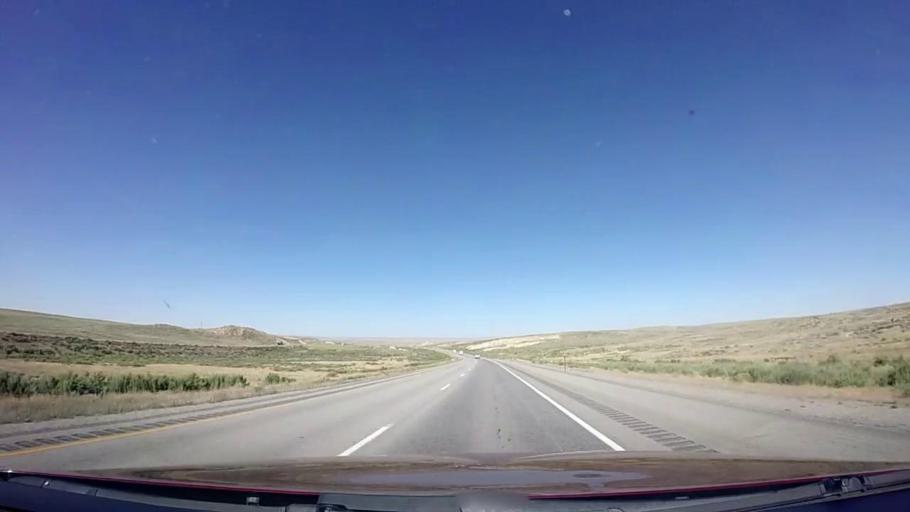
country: US
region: Wyoming
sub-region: Carbon County
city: Rawlins
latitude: 41.7893
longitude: -107.3849
